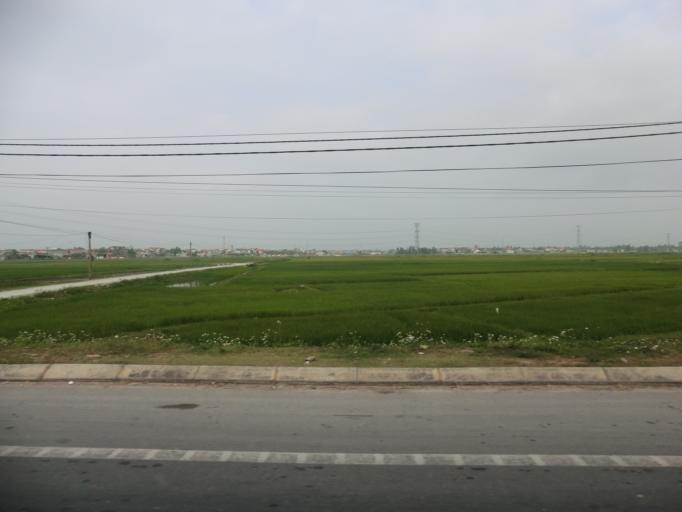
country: VN
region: Quang Binh
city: Ba Don
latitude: 17.7580
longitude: 106.4433
